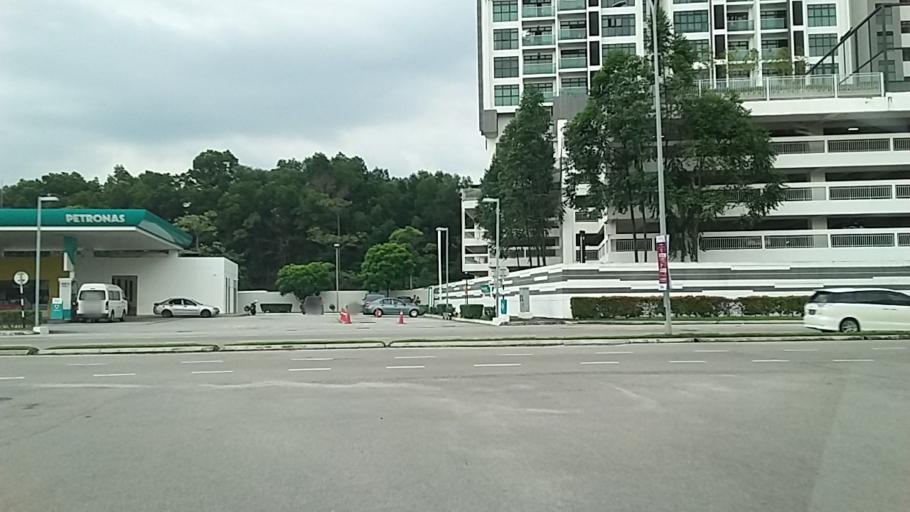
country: MY
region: Johor
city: Skudai
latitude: 1.4825
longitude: 103.6589
